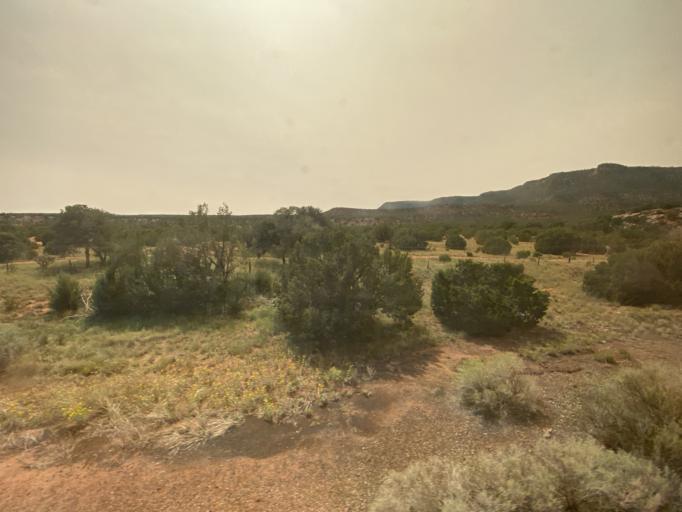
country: US
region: New Mexico
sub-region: San Miguel County
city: Pecos
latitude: 35.3962
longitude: -105.4908
